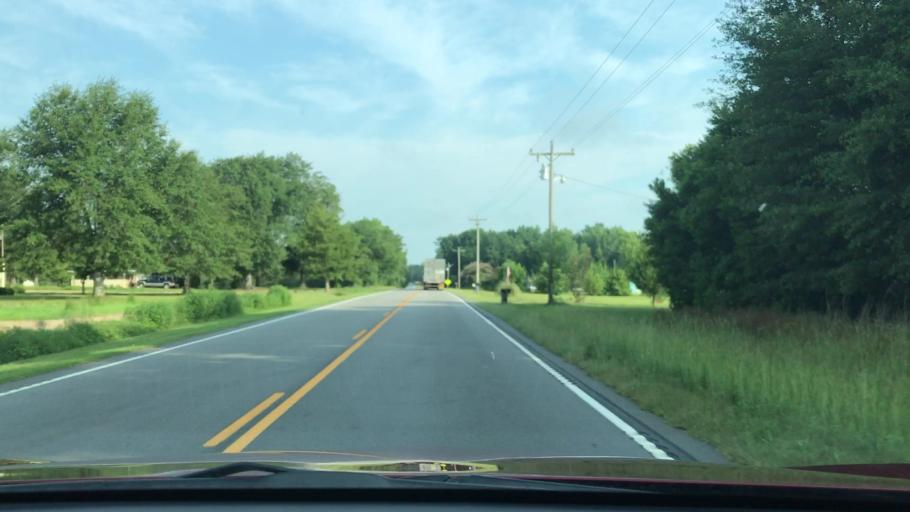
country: US
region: South Carolina
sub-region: Barnwell County
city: Blackville
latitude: 33.5550
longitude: -81.1629
